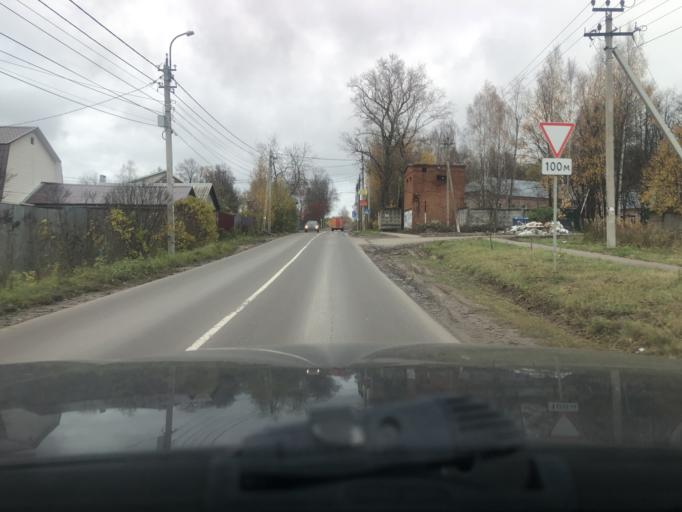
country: RU
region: Moskovskaya
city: Sergiyev Posad
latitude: 56.3053
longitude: 38.1093
